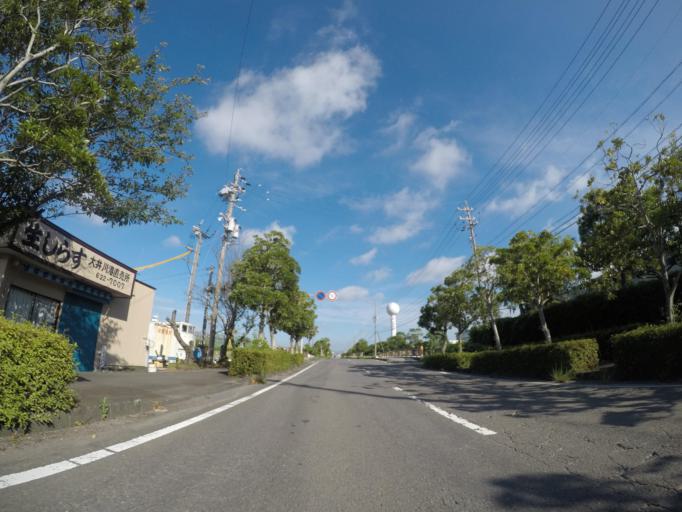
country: JP
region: Shizuoka
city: Fujieda
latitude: 34.7839
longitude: 138.2951
